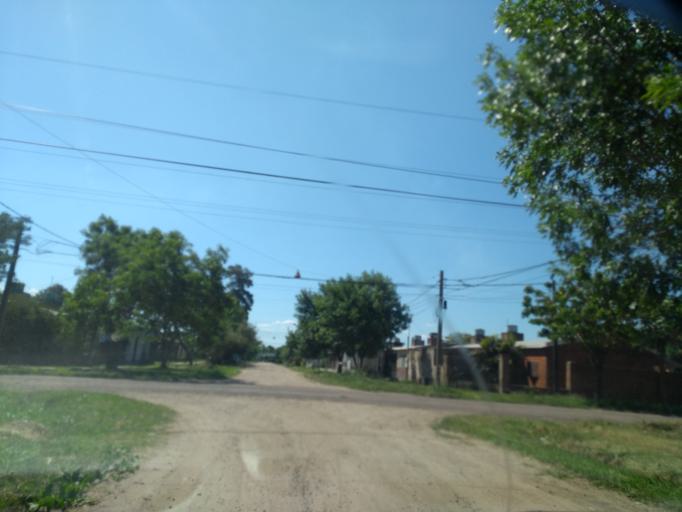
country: AR
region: Chaco
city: Fontana
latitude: -27.4124
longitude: -59.0401
